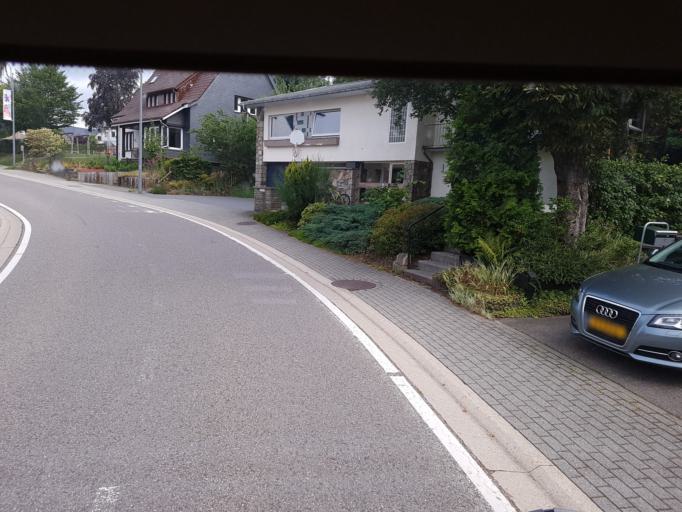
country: BE
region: Wallonia
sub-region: Province de Liege
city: Saint-Vith
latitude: 50.2813
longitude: 6.1234
